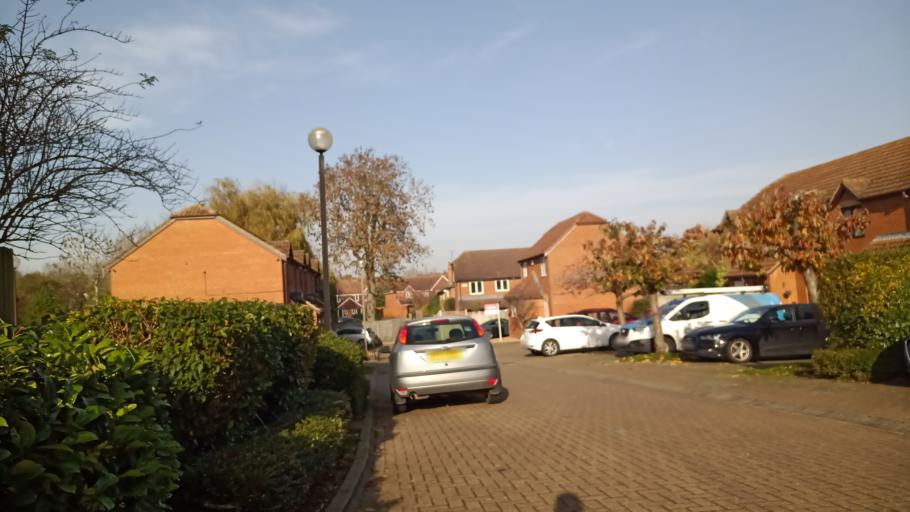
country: GB
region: England
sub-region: Milton Keynes
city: Shenley Church End
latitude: 52.0112
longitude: -0.7818
